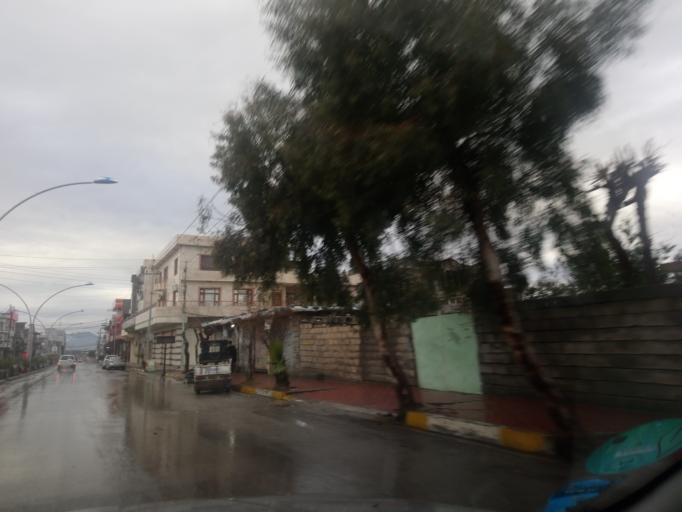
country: IQ
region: As Sulaymaniyah
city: Qeladize
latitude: 36.1801
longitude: 45.1330
